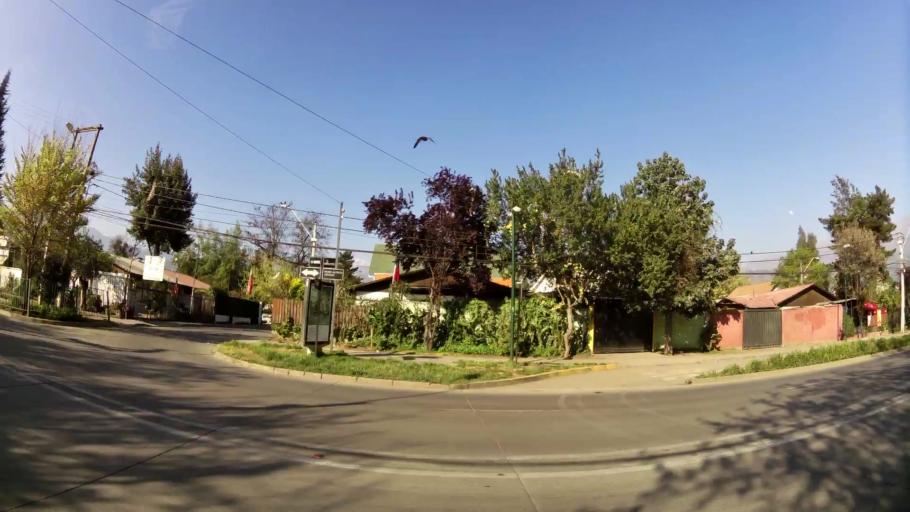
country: CL
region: Santiago Metropolitan
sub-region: Provincia de Santiago
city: Villa Presidente Frei, Nunoa, Santiago, Chile
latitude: -33.3578
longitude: -70.5101
